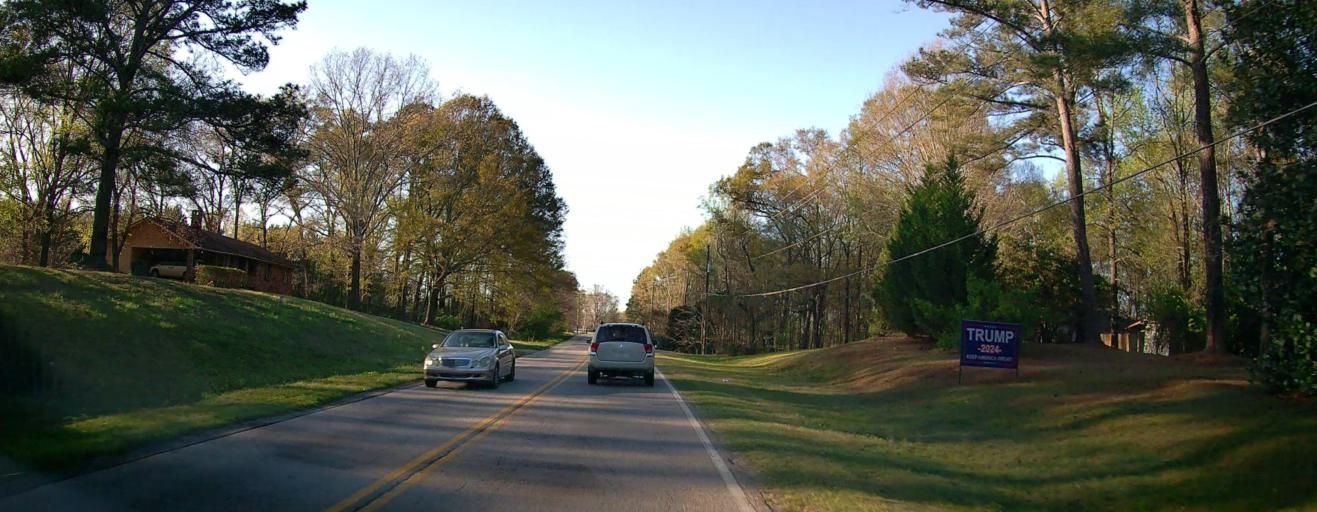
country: US
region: Georgia
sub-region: Newton County
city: Porterdale
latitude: 33.5689
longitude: -83.9033
